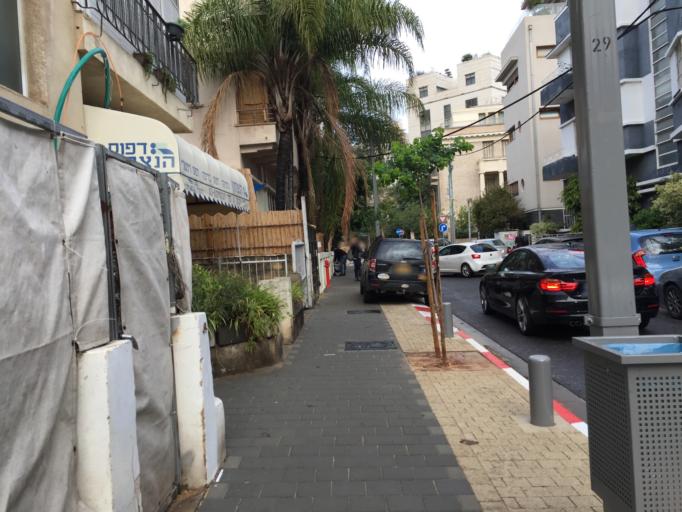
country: IL
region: Tel Aviv
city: Tel Aviv
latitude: 32.0667
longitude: 34.7725
